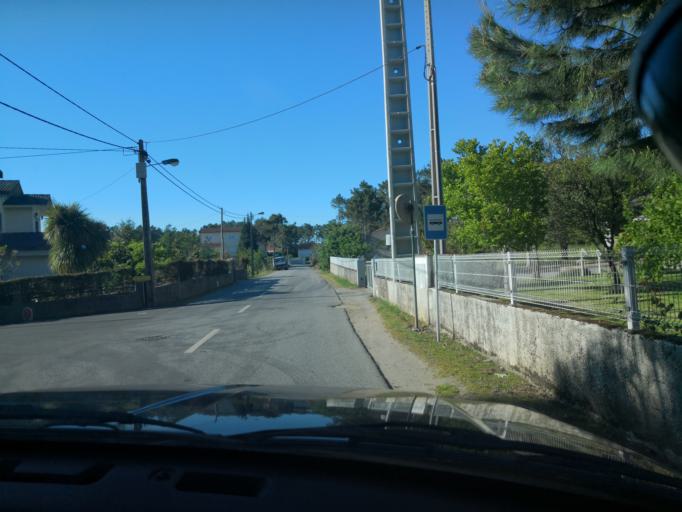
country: PT
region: Vila Real
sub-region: Vila Real
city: Vila Real
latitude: 41.2643
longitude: -7.7305
